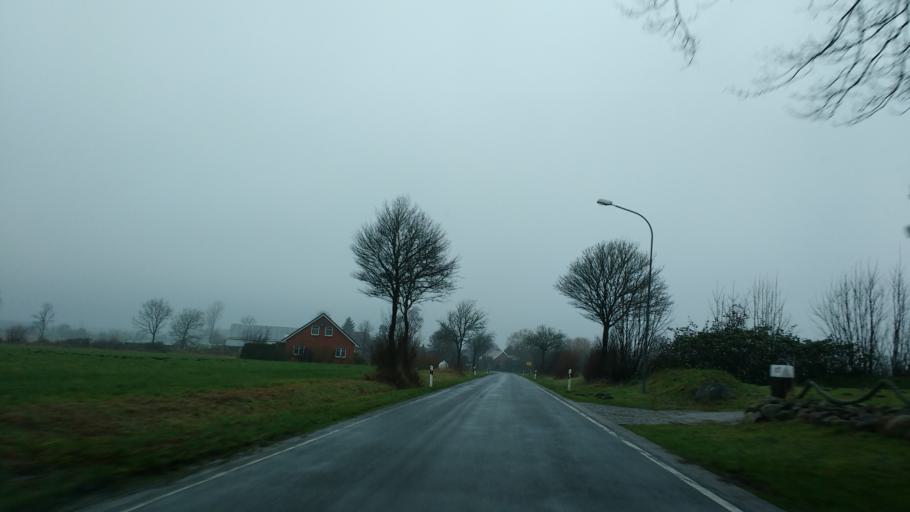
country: DE
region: Schleswig-Holstein
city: Luhnstedt
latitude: 54.1620
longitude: 9.7019
